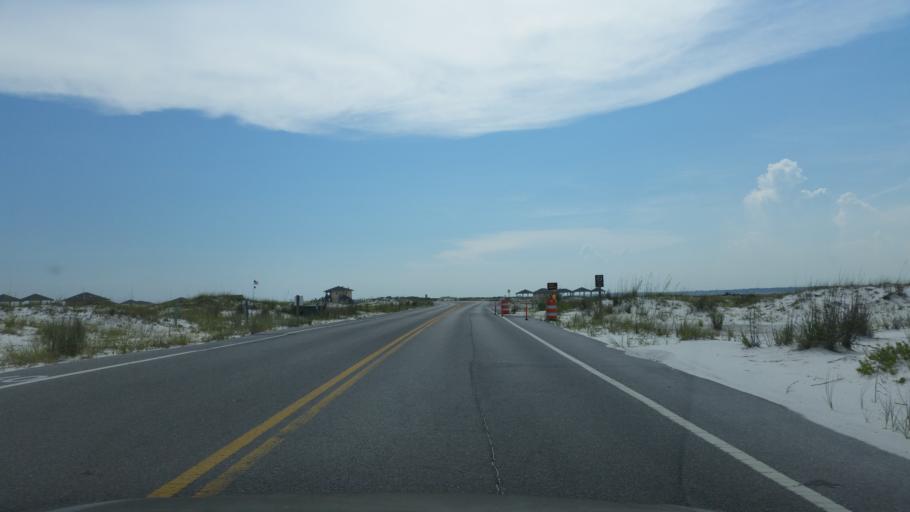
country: US
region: Florida
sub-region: Santa Rosa County
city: Woodlawn Beach
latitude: 30.3648
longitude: -86.9640
